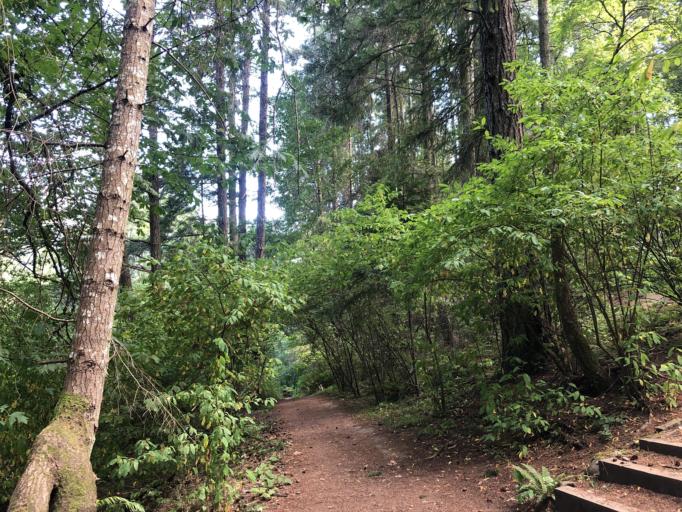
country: CA
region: British Columbia
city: Metchosin
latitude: 48.3645
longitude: -123.5375
